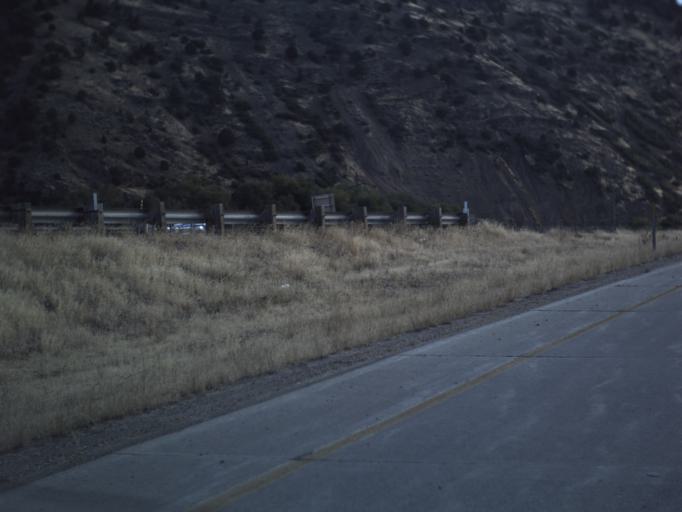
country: US
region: Utah
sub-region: Morgan County
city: Morgan
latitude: 41.0508
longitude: -111.6237
